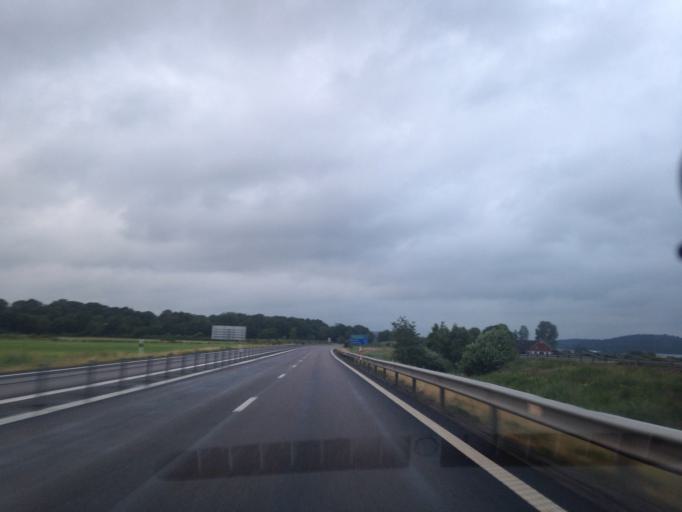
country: SE
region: Halland
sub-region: Varbergs Kommun
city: Varberg
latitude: 57.1483
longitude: 12.2687
